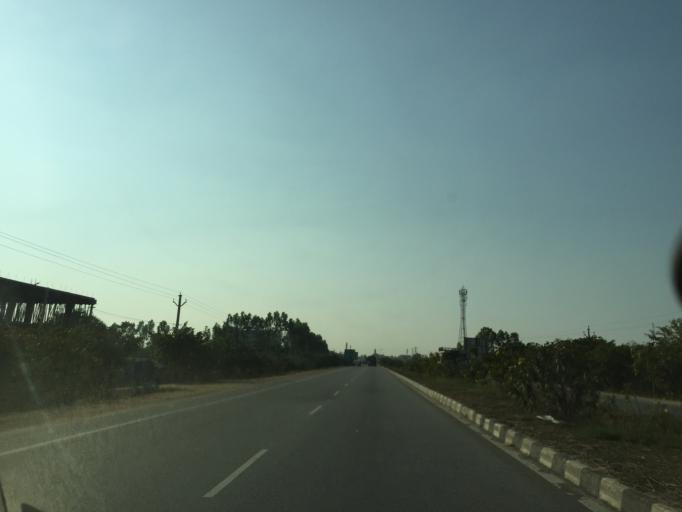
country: IN
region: Telangana
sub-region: Nalgonda
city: Bhongir
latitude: 17.5021
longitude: 78.8783
